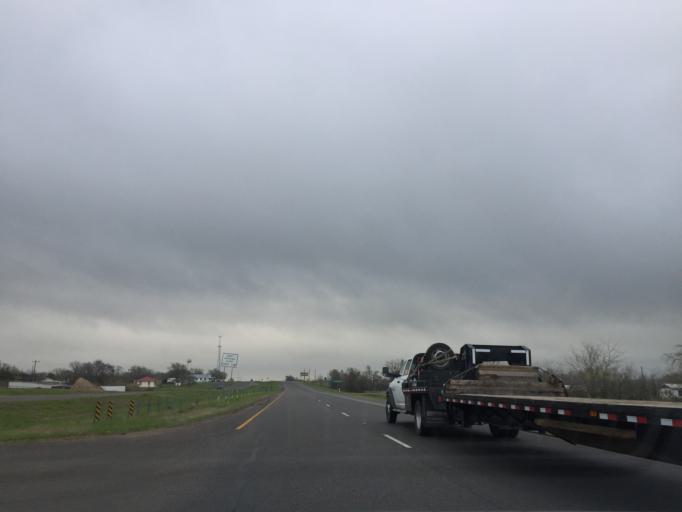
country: US
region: Texas
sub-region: Travis County
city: Garfield
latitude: 30.1882
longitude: -97.5661
